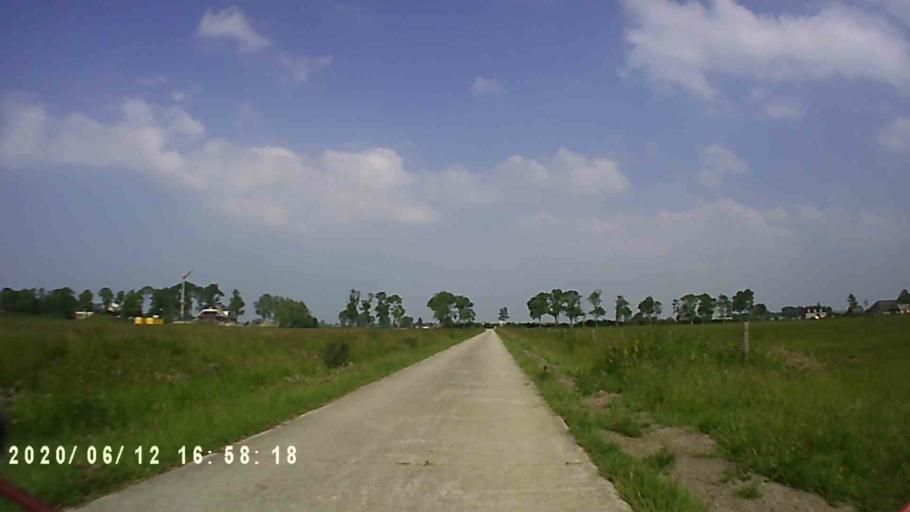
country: NL
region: Groningen
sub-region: Gemeente Groningen
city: Korrewegwijk
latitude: 53.2646
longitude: 6.5627
